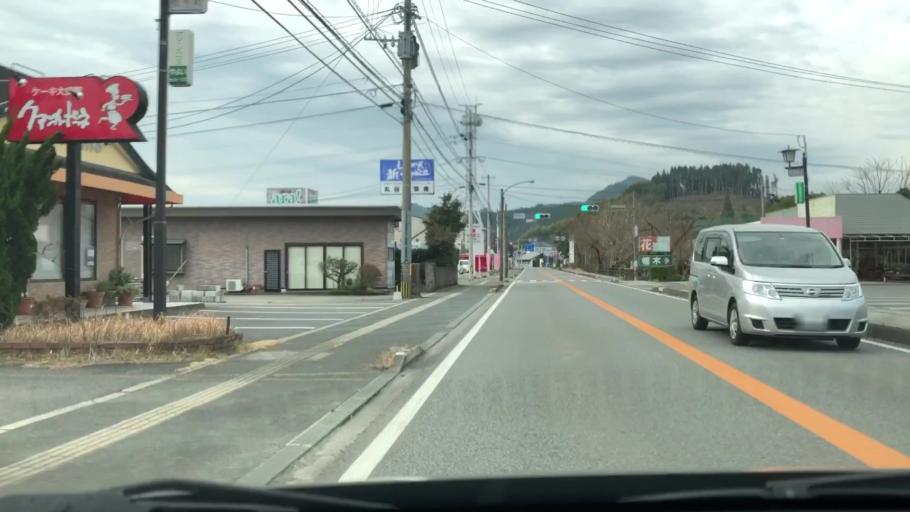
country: JP
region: Oita
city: Saiki
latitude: 32.9712
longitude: 131.8404
